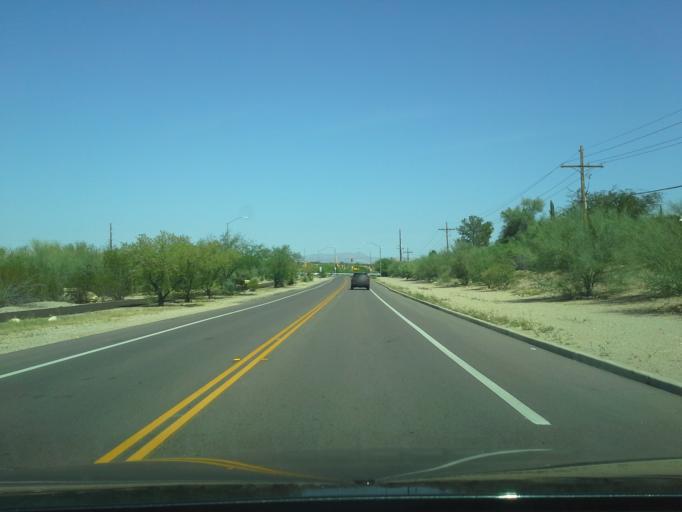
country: US
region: Arizona
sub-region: Pima County
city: Flowing Wells
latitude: 32.2484
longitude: -111.0204
